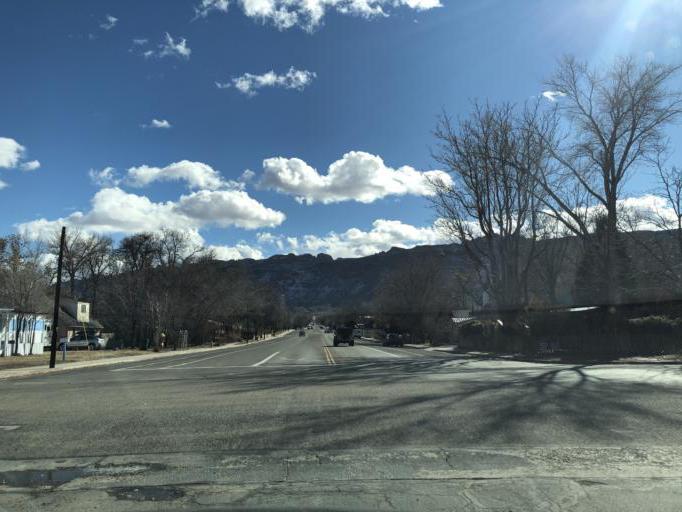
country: US
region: Utah
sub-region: Grand County
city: Moab
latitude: 38.5751
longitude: -109.5430
